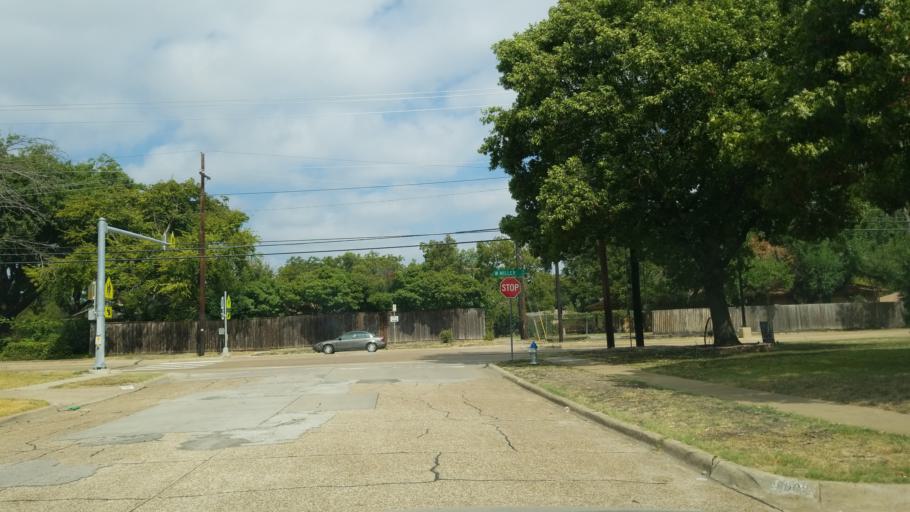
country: US
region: Texas
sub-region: Dallas County
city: Garland
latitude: 32.8940
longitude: -96.6597
